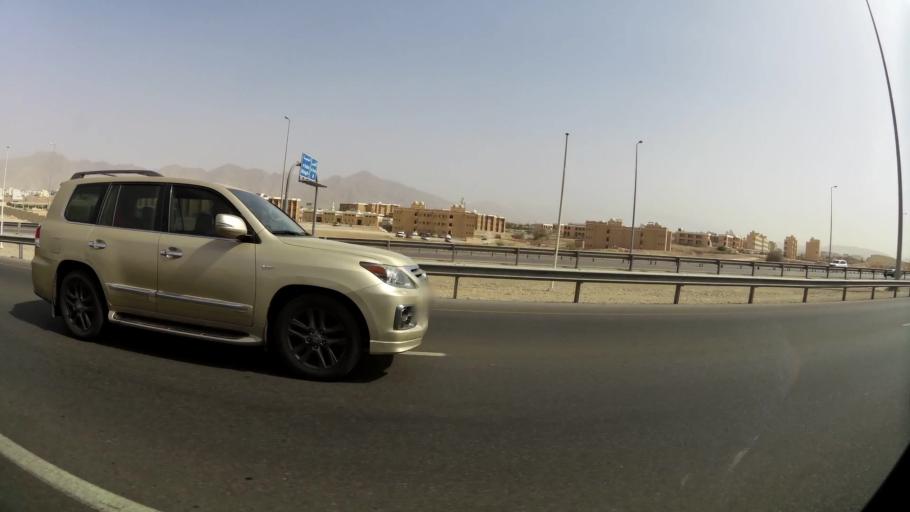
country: OM
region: Muhafazat Masqat
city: Bawshar
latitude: 23.5677
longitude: 58.3740
